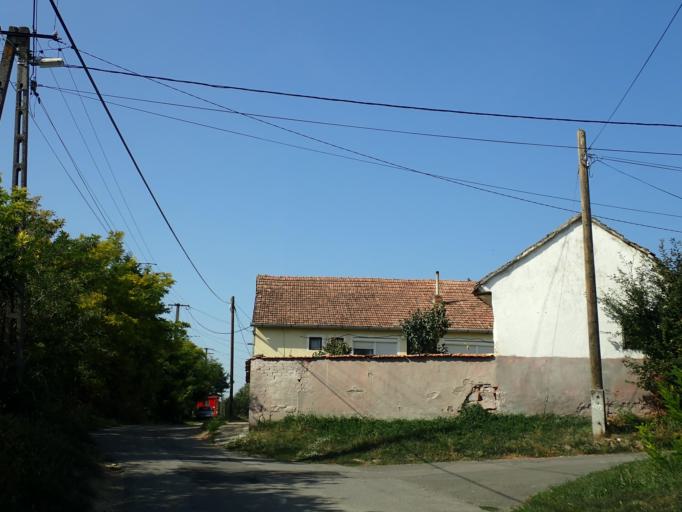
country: HU
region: Baranya
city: Boly
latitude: 45.9983
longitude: 18.5109
